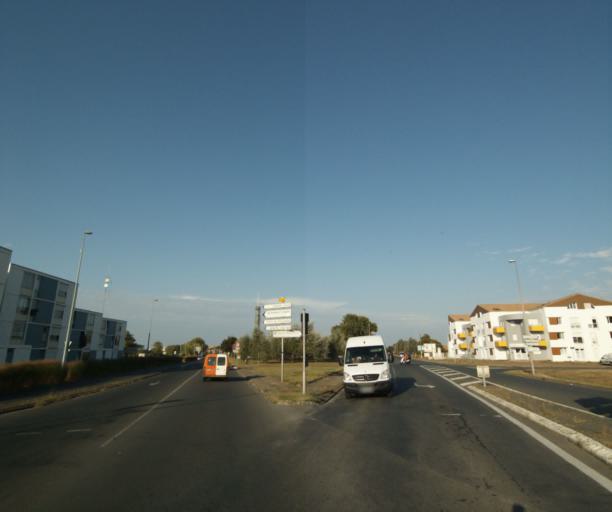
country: FR
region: Poitou-Charentes
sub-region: Departement de la Charente-Maritime
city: Breuil-Magne
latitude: 45.9504
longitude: -0.9452
